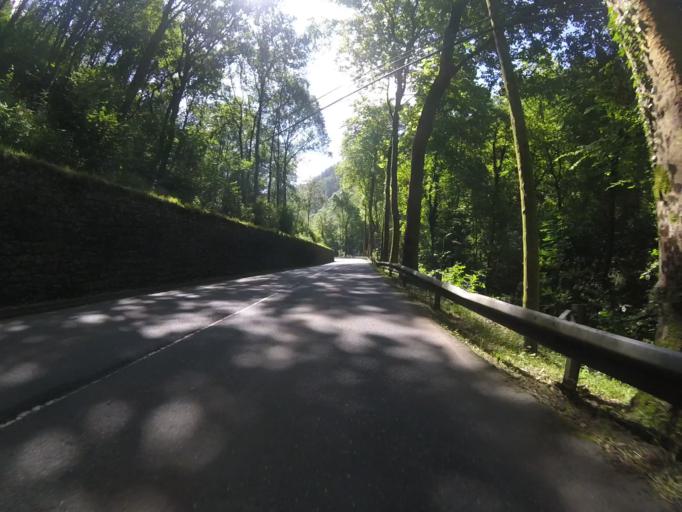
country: ES
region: Basque Country
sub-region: Provincia de Guipuzcoa
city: Azpeitia
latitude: 43.1790
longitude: -2.2412
